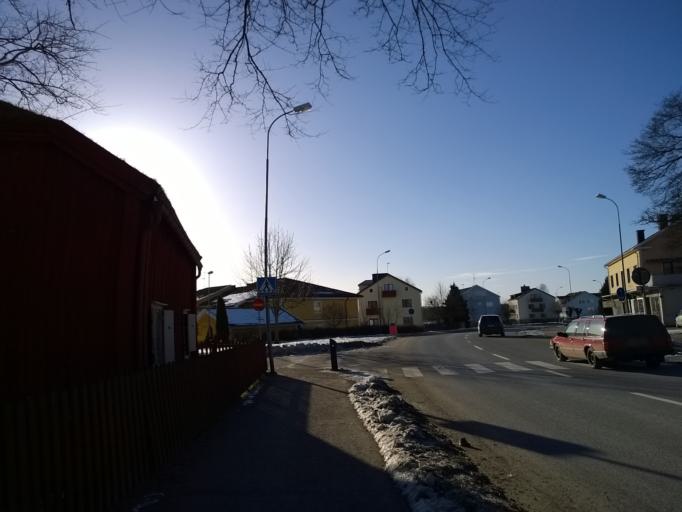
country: SE
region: Kronoberg
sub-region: Alvesta Kommun
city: Alvesta
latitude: 56.8982
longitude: 14.5522
